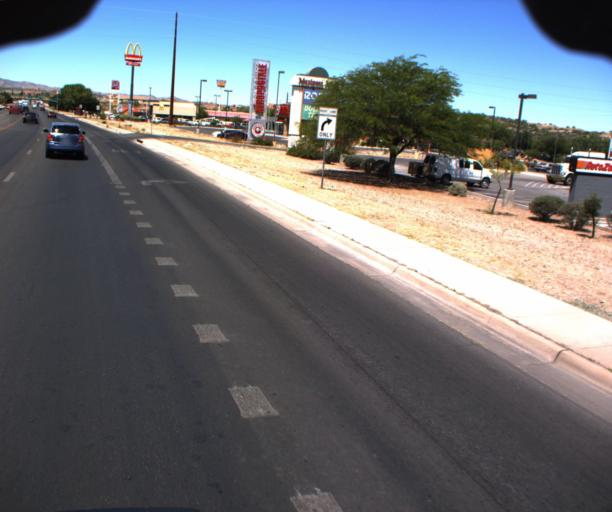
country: US
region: Arizona
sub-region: Santa Cruz County
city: Nogales
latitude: 31.3668
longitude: -110.9371
